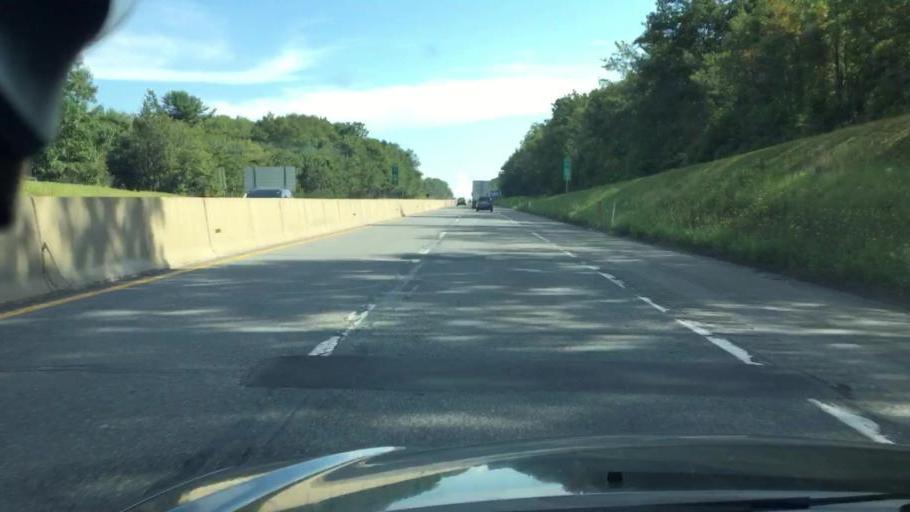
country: US
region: Pennsylvania
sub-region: Carbon County
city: Towamensing Trails
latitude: 40.9971
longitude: -75.6332
